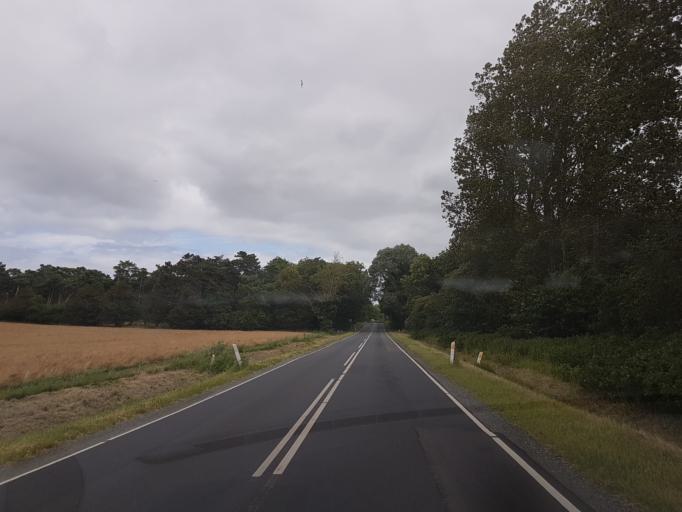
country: DK
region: South Denmark
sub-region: Nordfyns Kommune
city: Bogense
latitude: 55.5695
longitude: 10.1920
